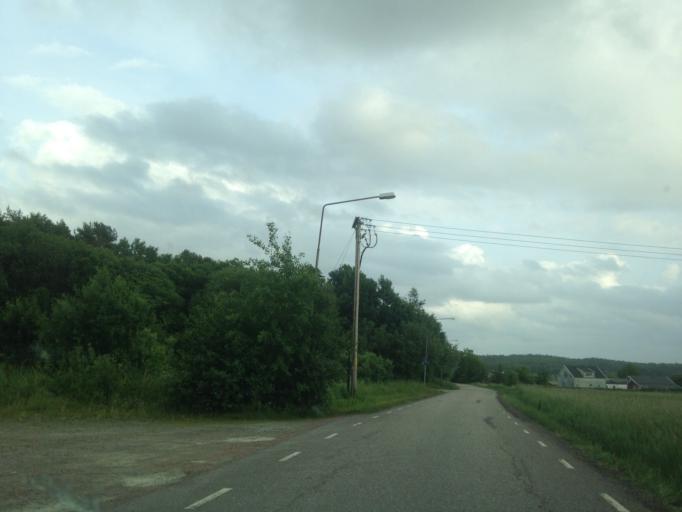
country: SE
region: Vaestra Goetaland
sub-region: Kungalvs Kommun
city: Kungalv
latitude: 57.8001
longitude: 11.9205
